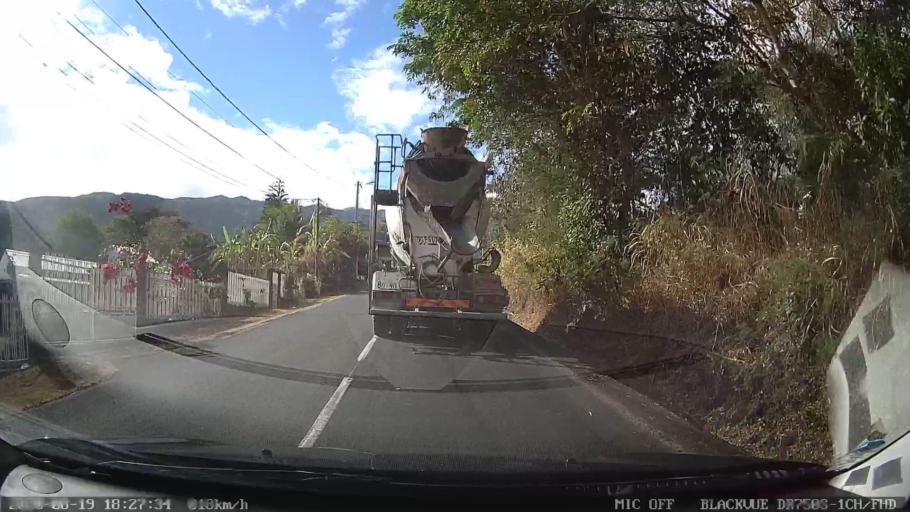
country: RE
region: Reunion
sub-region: Reunion
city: La Possession
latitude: -20.9555
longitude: 55.3503
